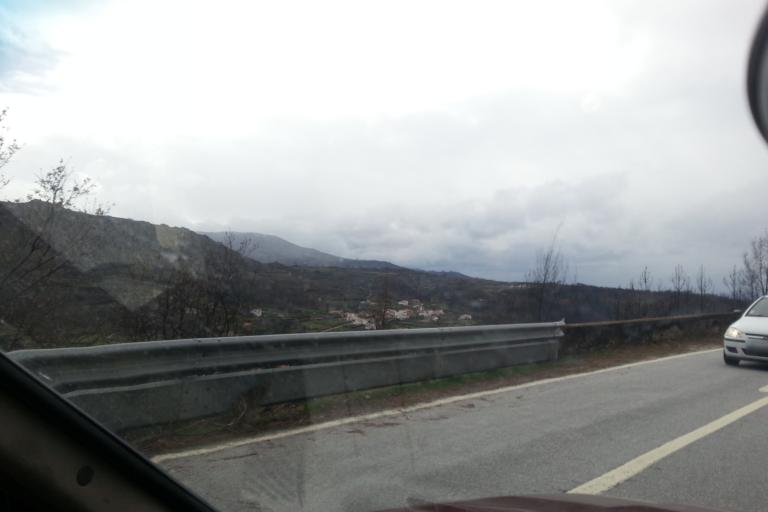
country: PT
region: Guarda
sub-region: Manteigas
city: Manteigas
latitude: 40.4737
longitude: -7.5951
